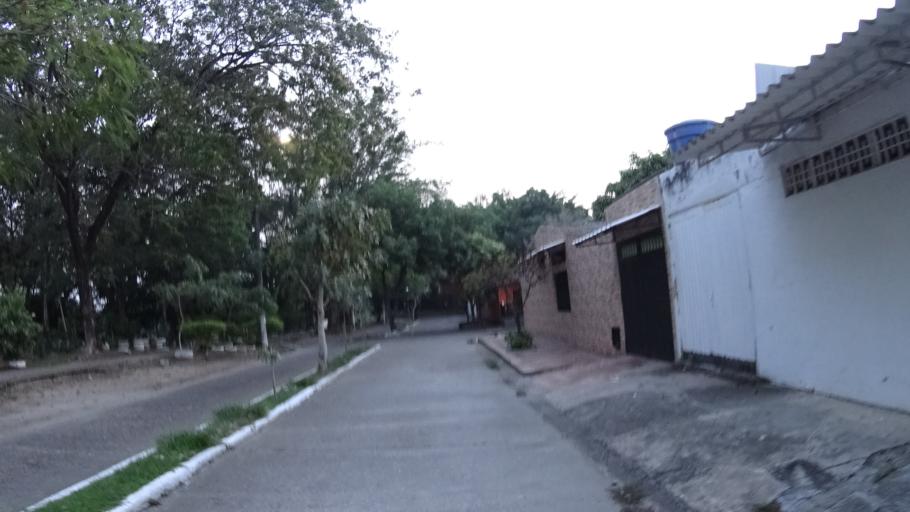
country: CO
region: Caldas
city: La Dorada
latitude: 5.4429
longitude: -74.6593
